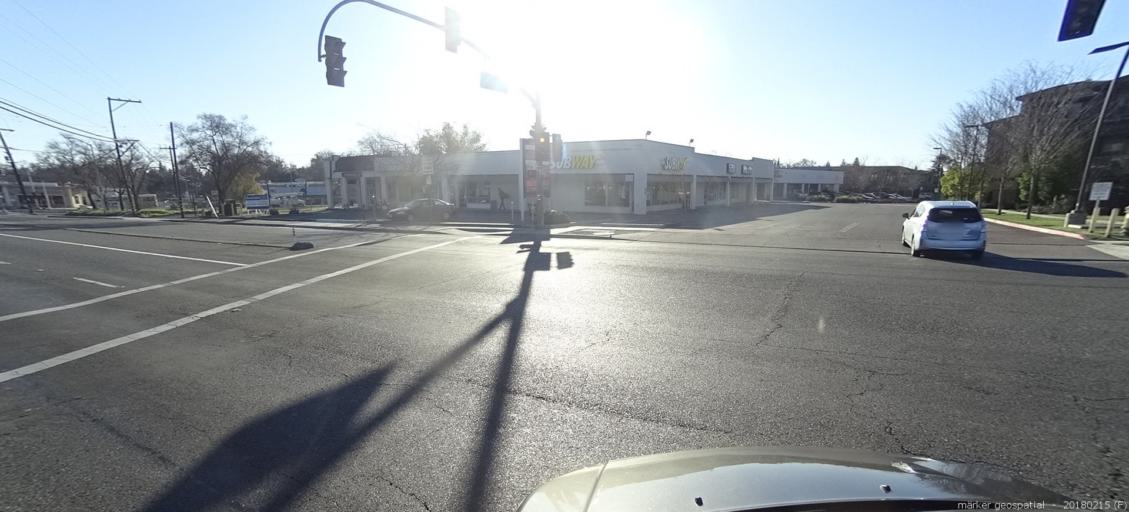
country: US
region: California
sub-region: Sacramento County
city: Foothill Farms
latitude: 38.6679
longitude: -121.3382
